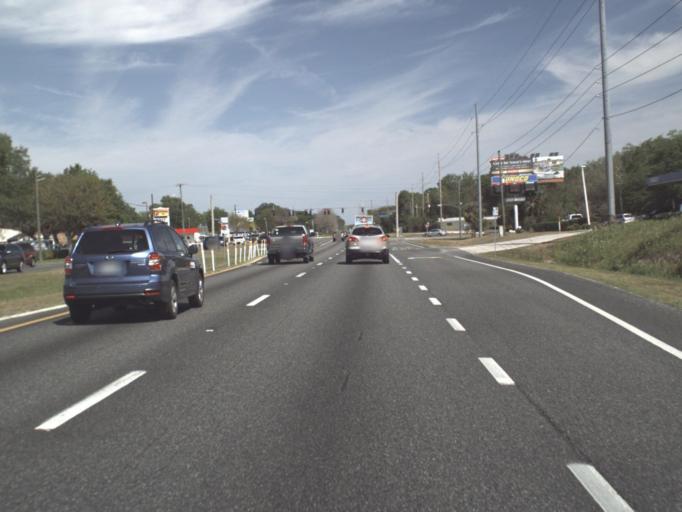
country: US
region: Florida
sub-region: Lake County
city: Lady Lake
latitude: 28.9073
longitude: -81.9166
